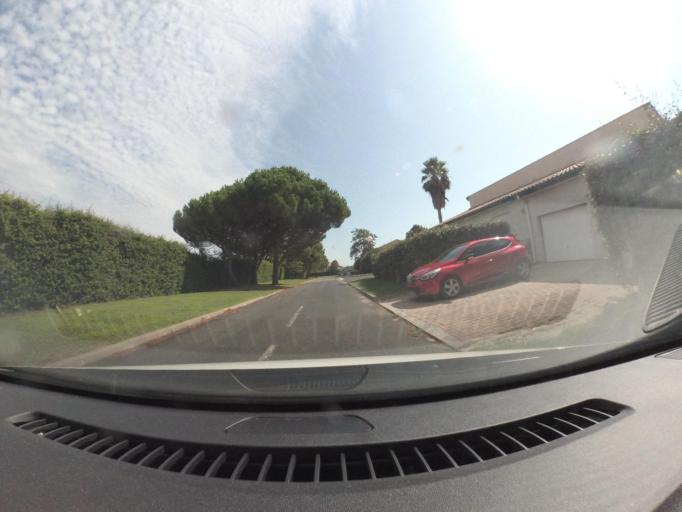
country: FR
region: Languedoc-Roussillon
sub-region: Departement de l'Herault
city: Baillargues
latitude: 43.6492
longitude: 4.0115
